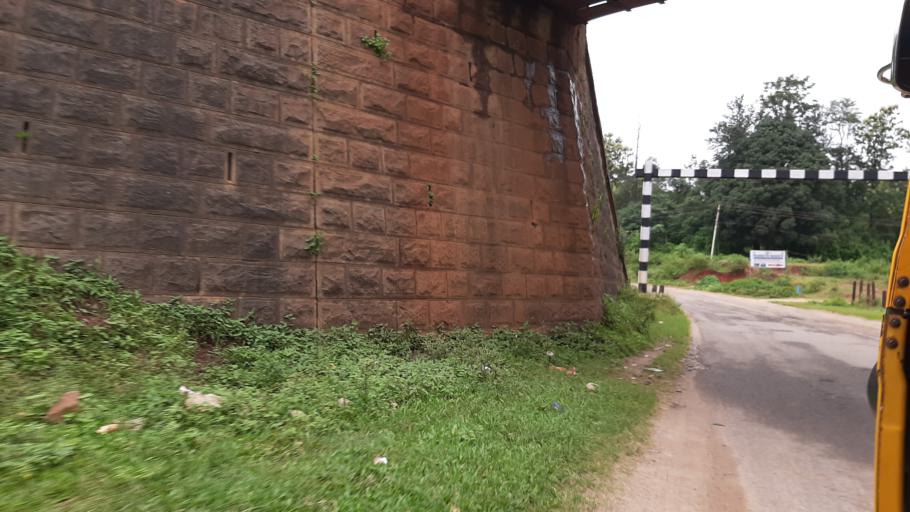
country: IN
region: Andhra Pradesh
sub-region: Vizianagaram District
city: Salur
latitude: 18.3048
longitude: 82.9076
